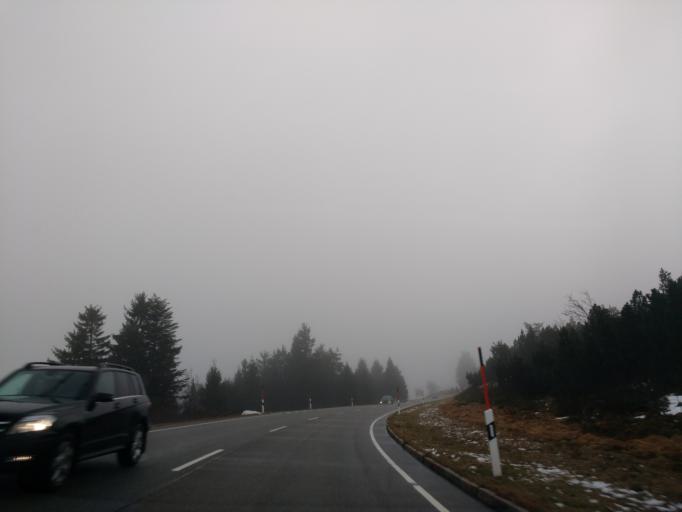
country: DE
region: Baden-Wuerttemberg
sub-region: Freiburg Region
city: Seebach
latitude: 48.5384
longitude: 8.2228
